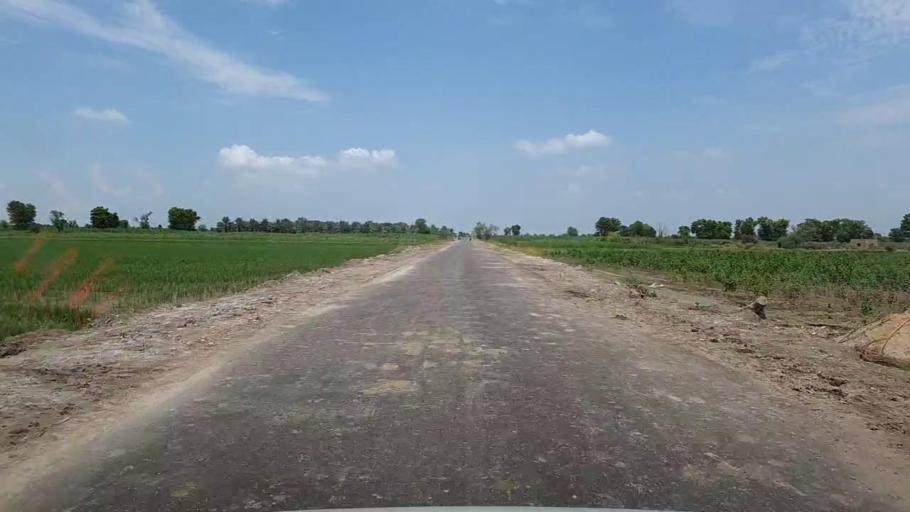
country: PK
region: Sindh
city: Bhiria
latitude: 26.9308
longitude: 68.2134
